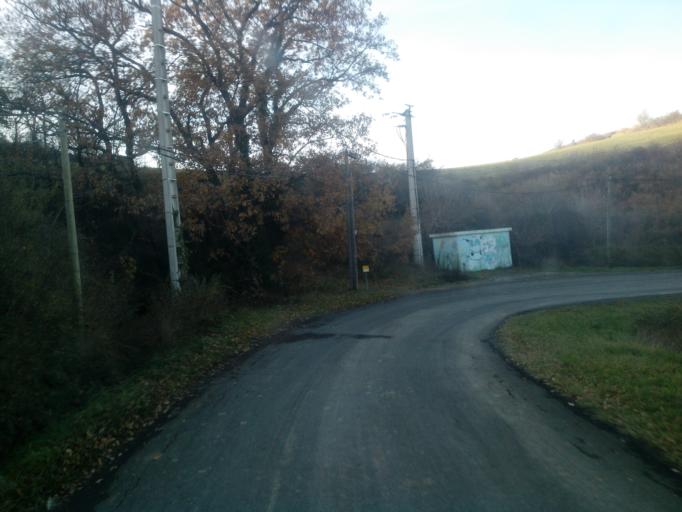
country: FR
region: Languedoc-Roussillon
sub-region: Departement de l'Aude
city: Couiza
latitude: 42.8924
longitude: 2.3137
